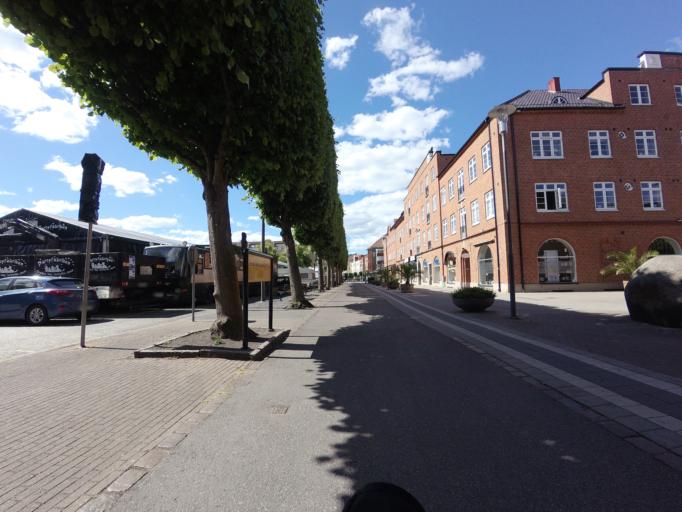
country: SE
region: Skane
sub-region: Trelleborgs Kommun
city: Trelleborg
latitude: 55.3759
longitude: 13.1575
